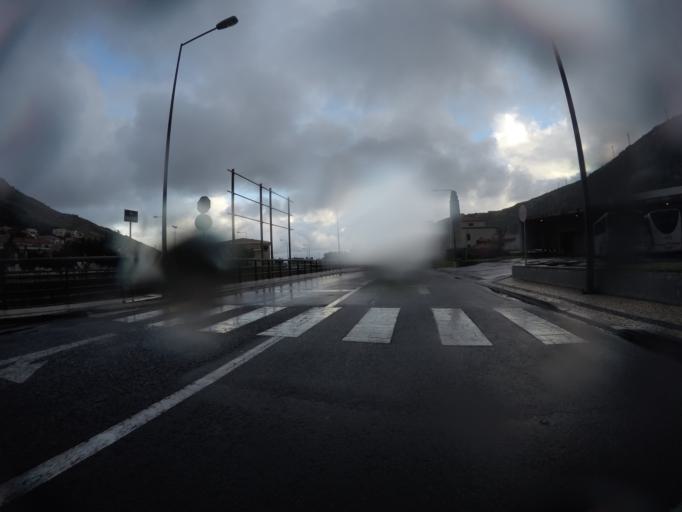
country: PT
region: Madeira
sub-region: Machico
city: Machico
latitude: 32.7213
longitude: -16.7685
